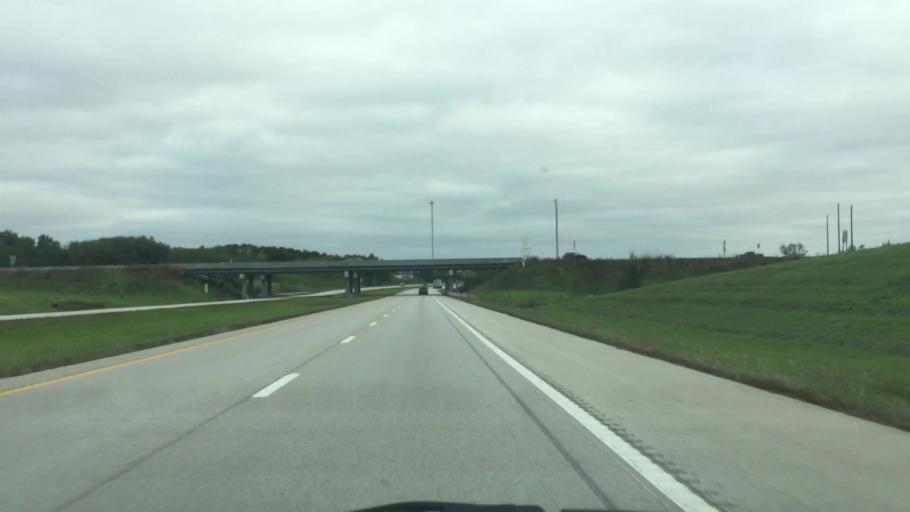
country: US
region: Missouri
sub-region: Clinton County
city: Cameron
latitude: 39.7521
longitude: -94.2197
